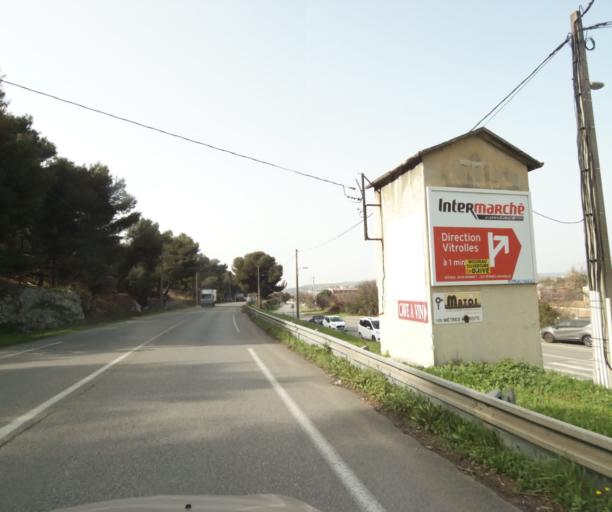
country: FR
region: Provence-Alpes-Cote d'Azur
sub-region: Departement des Bouches-du-Rhone
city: Les Pennes-Mirabeau
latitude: 43.4115
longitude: 5.3048
